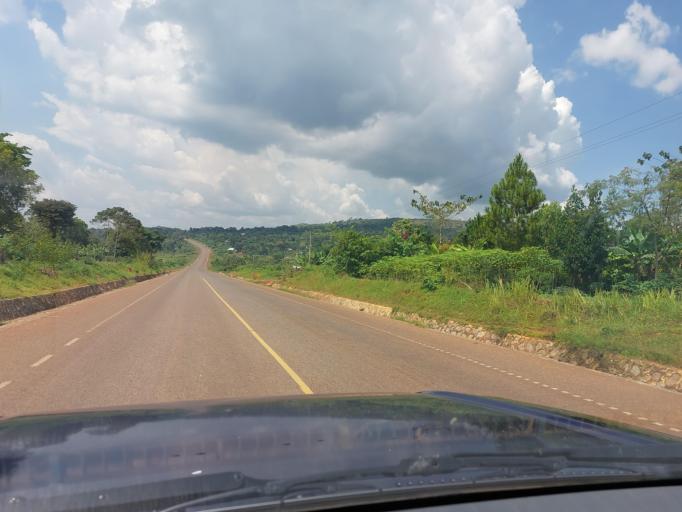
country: UG
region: Central Region
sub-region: Buikwe District
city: Buikwe
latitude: 0.3168
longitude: 33.1104
